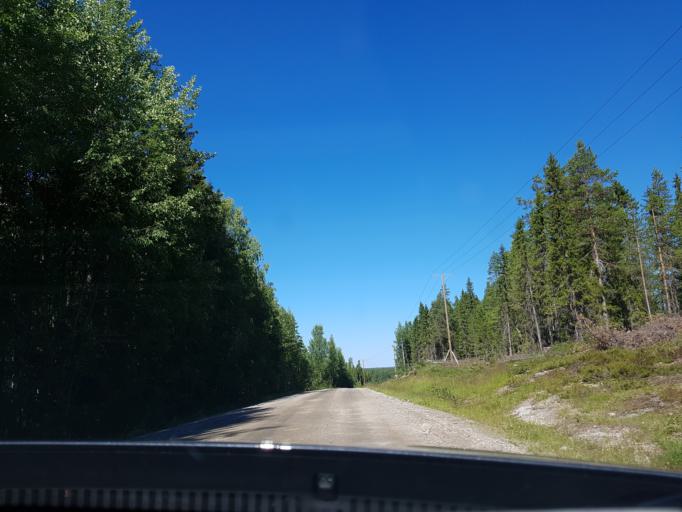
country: FI
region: Kainuu
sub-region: Kehys-Kainuu
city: Kuhmo
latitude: 64.1706
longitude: 29.6422
